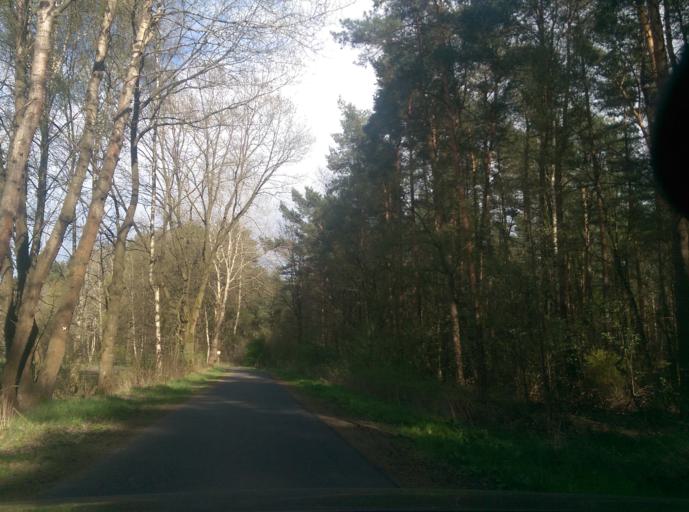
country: DE
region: Lower Saxony
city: Garbsen-Mitte
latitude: 52.5220
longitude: 9.6331
